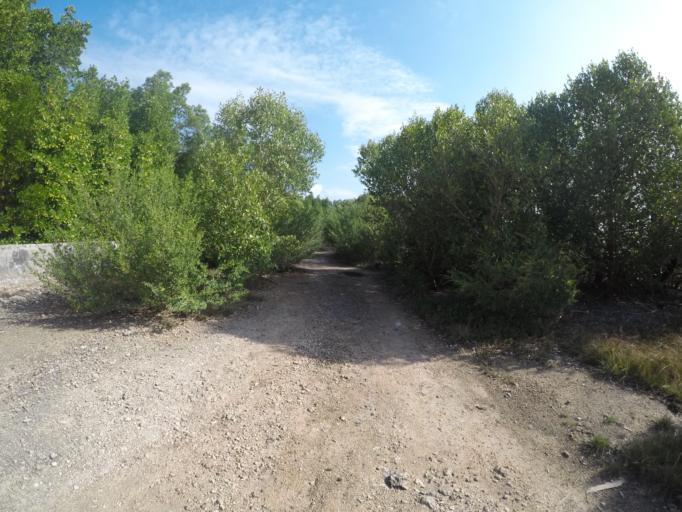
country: TZ
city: Kiwengwa
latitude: -6.1453
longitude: 39.4898
